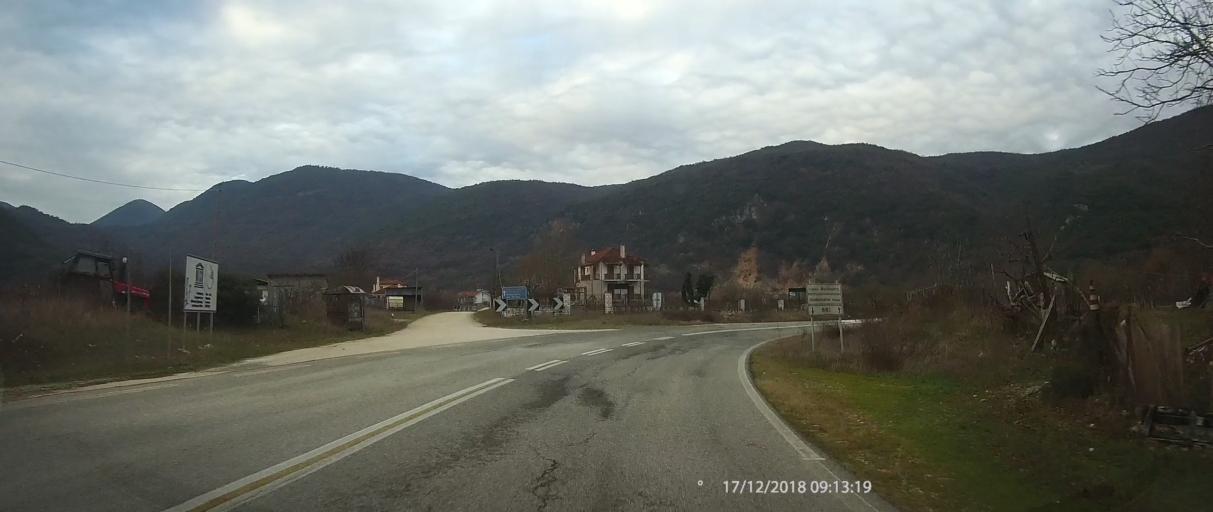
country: GR
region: Epirus
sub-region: Nomos Ioanninon
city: Kalpaki
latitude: 39.9735
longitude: 20.6603
